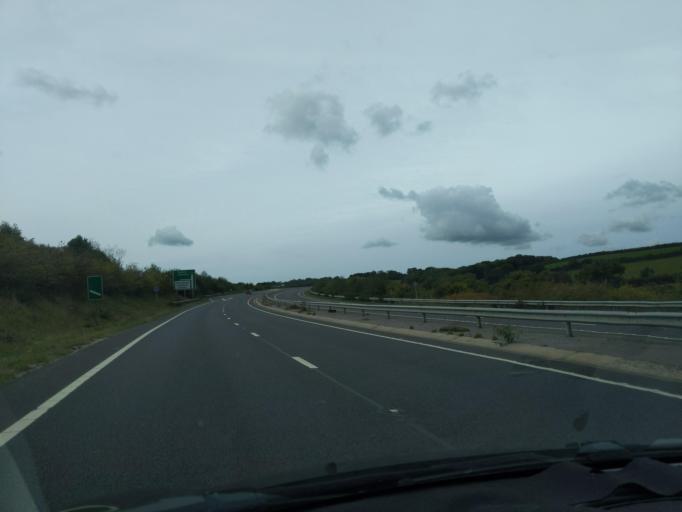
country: GB
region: England
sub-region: Cornwall
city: Liskeard
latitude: 50.4576
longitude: -4.5024
